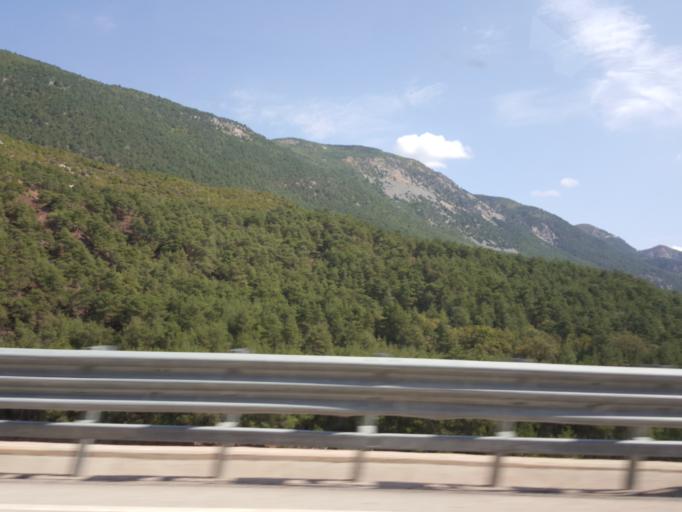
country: TR
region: Tokat
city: Basciftlik
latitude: 40.4390
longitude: 37.1017
